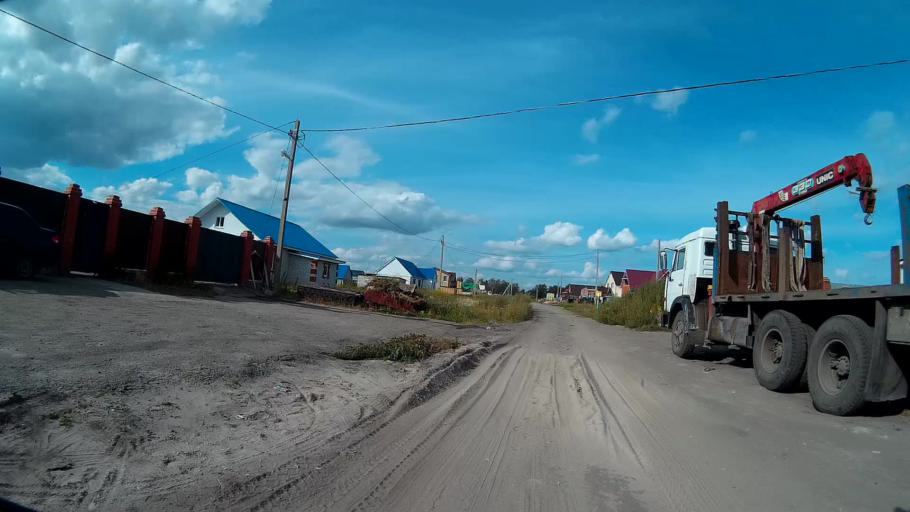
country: RU
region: Ulyanovsk
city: Isheyevka
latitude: 54.2868
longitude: 48.2158
